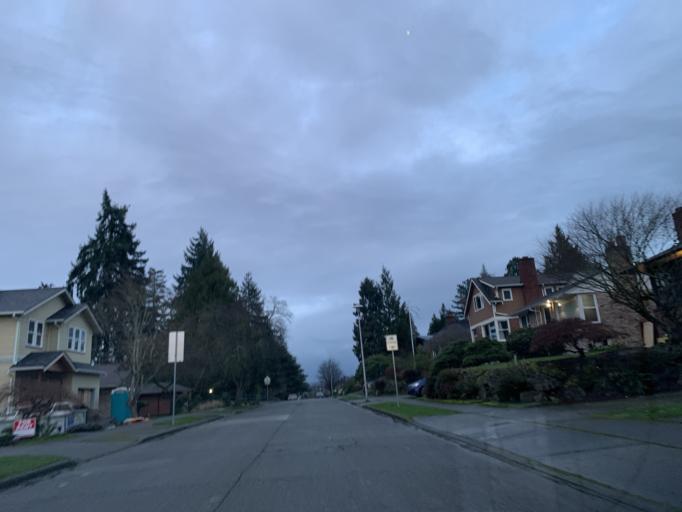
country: US
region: Washington
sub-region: King County
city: Yarrow Point
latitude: 47.6728
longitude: -122.2630
